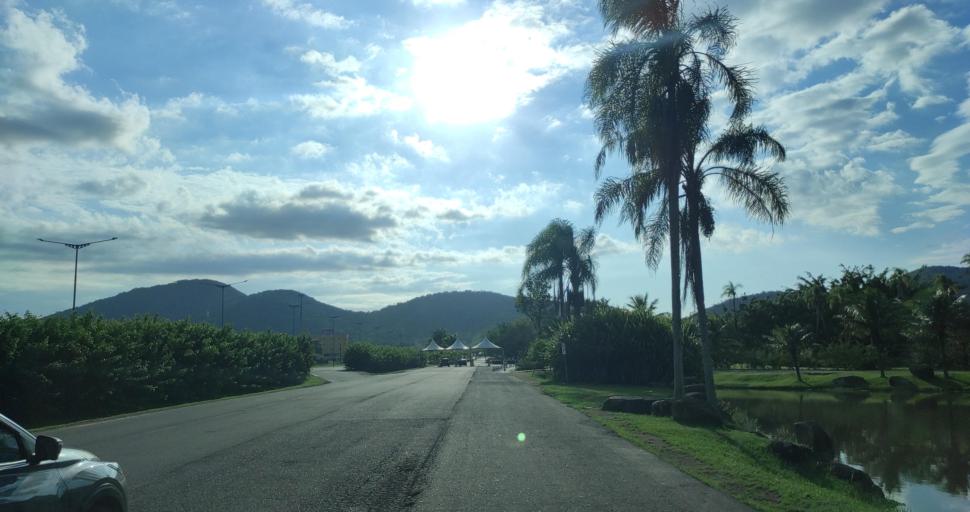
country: BR
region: Santa Catarina
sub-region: Penha
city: Penha
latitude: -26.7986
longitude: -48.6179
